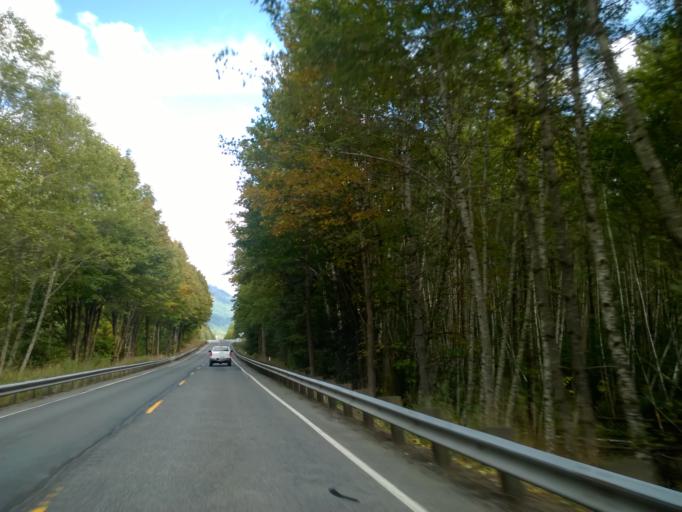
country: US
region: Washington
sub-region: Snohomish County
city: Gold Bar
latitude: 47.7152
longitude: -121.2617
